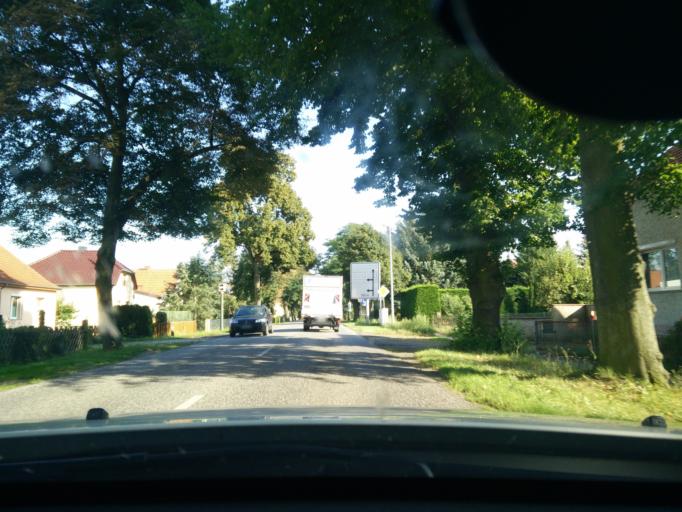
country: DE
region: Brandenburg
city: Gross Kreutz
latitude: 52.3962
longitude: 12.8286
